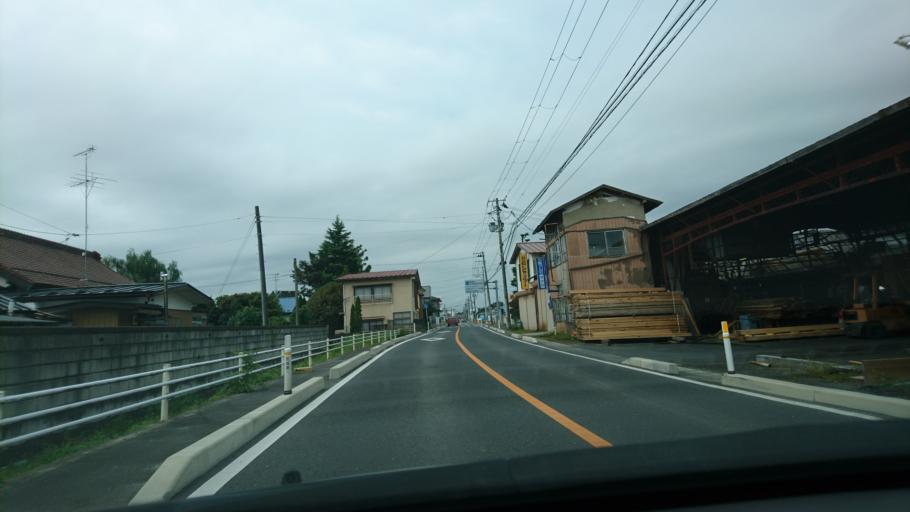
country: JP
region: Iwate
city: Ichinoseki
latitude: 38.7551
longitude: 141.0684
